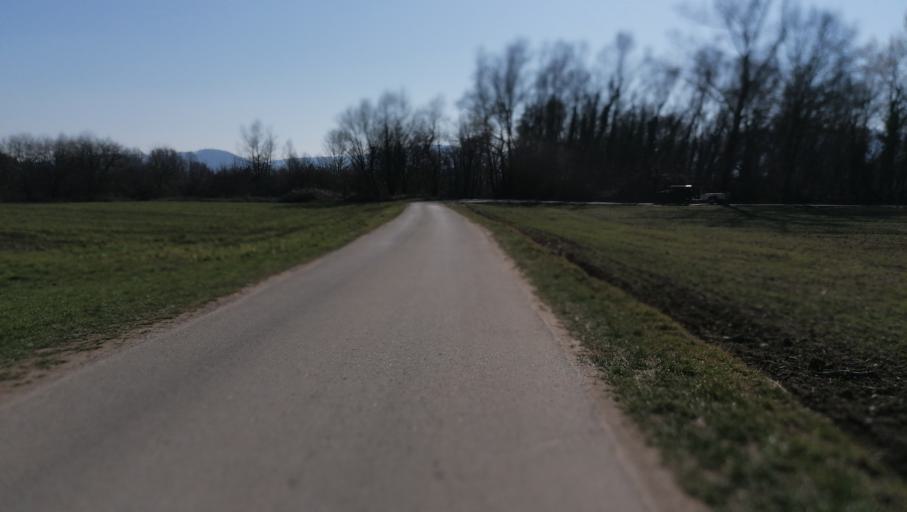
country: CH
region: Aargau
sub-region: Bezirk Rheinfelden
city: Mumpf
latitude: 47.5754
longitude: 7.9172
